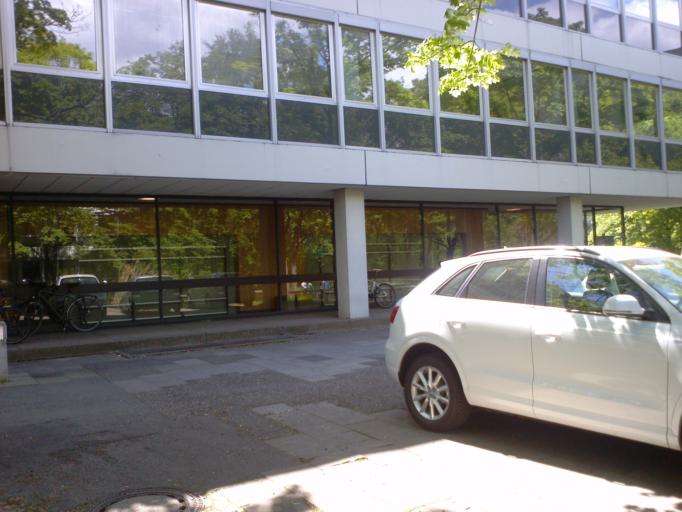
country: DE
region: Baden-Wuerttemberg
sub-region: Karlsruhe Region
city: Karlsruhe
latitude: 49.0130
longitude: 8.4108
